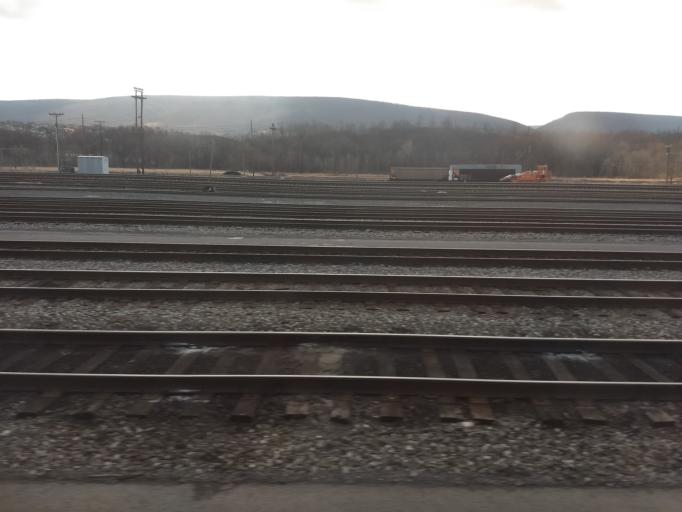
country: US
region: Pennsylvania
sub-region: Blair County
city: Altoona
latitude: 40.5355
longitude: -78.3801
